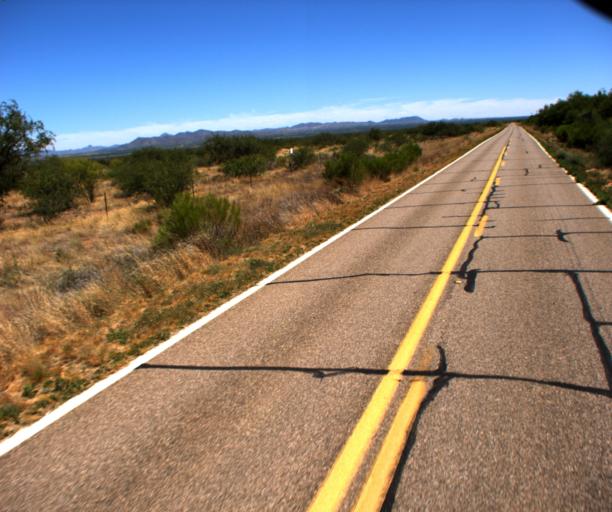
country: US
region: Arizona
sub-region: Pima County
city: Three Points
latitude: 31.7043
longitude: -111.4876
